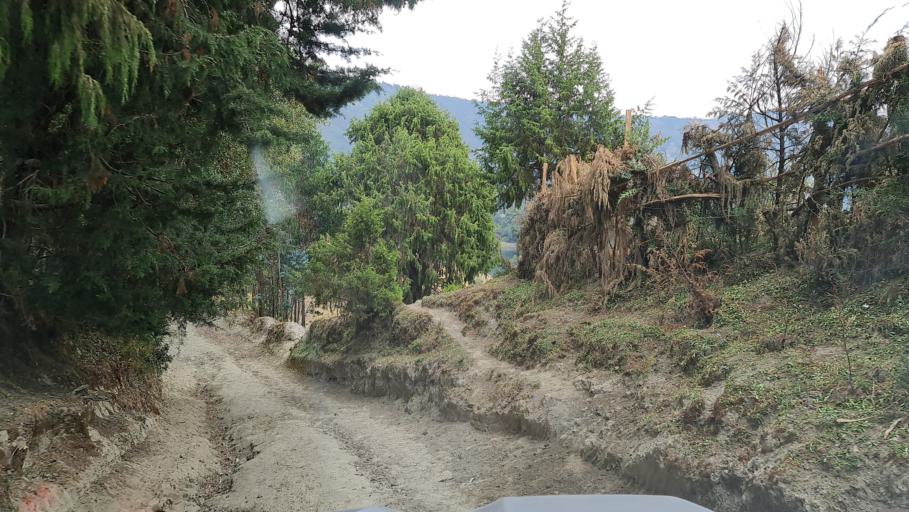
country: ET
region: Oromiya
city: Hagere Hiywet
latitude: 8.7989
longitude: 37.8910
